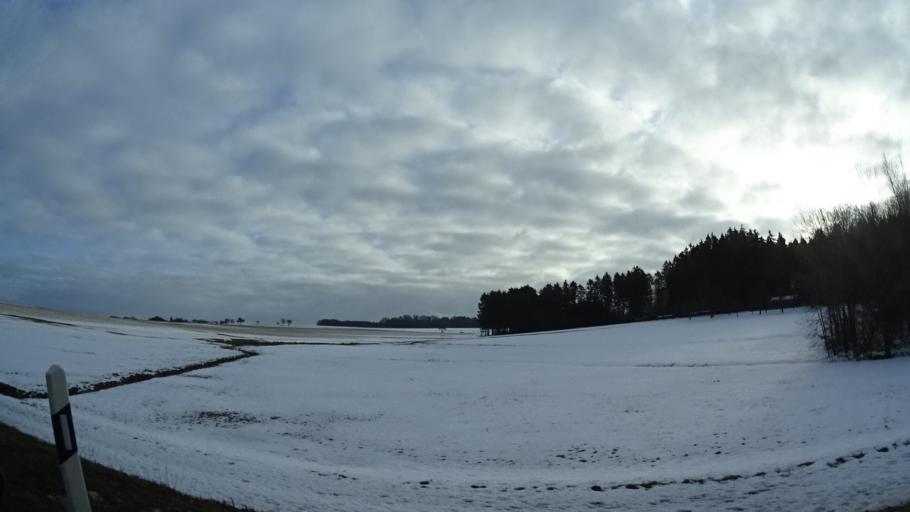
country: DE
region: Baden-Wuerttemberg
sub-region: Karlsruhe Region
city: Fahrenbach
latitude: 49.4973
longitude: 9.1476
